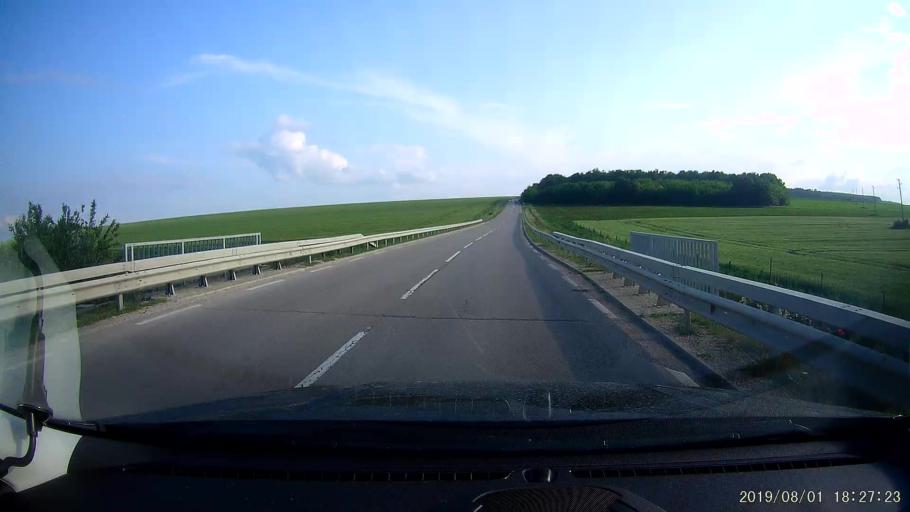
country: BG
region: Shumen
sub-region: Obshtina Venets
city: Venets
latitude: 43.5882
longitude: 26.9829
